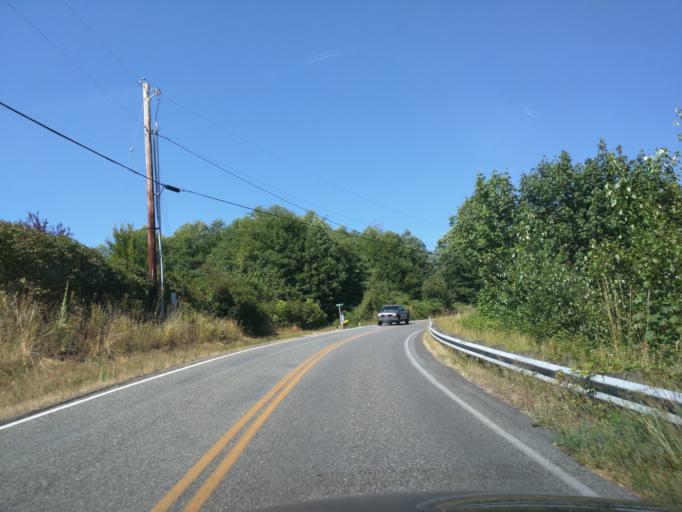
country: US
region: Washington
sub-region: Whatcom County
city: Nooksack
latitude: 48.9287
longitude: -122.2644
